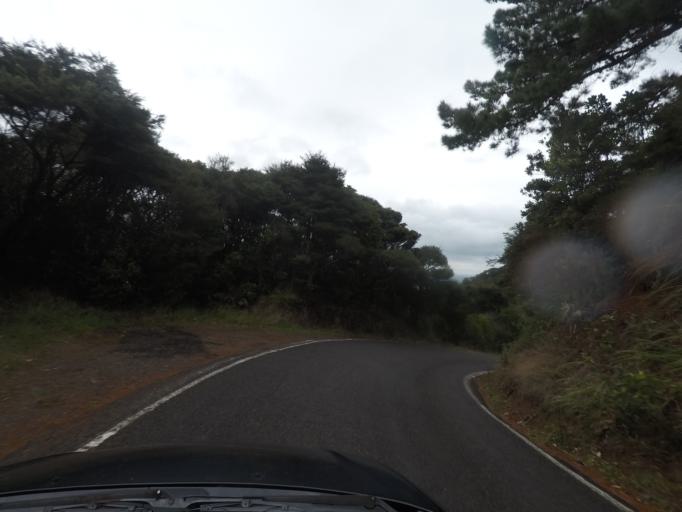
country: NZ
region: Auckland
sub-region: Auckland
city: Muriwai Beach
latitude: -36.9690
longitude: 174.4885
